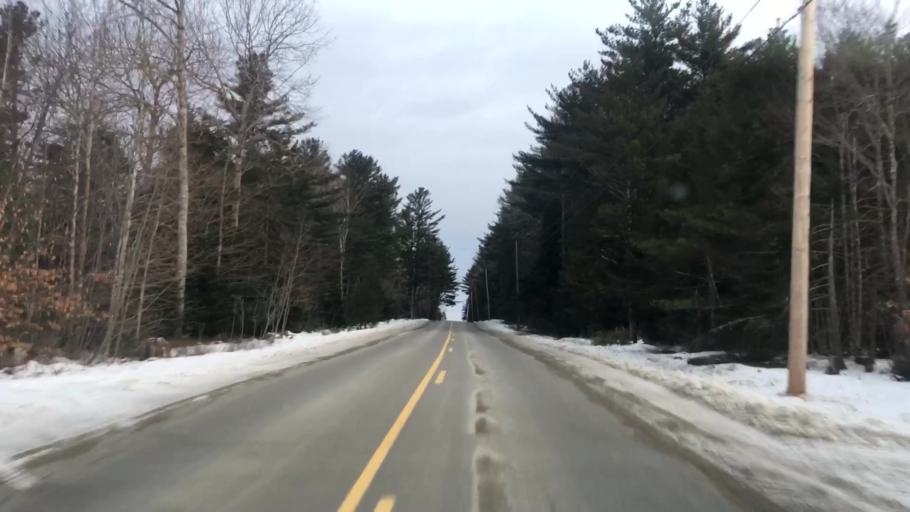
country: US
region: Maine
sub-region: Hancock County
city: Franklin
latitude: 44.7636
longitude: -68.3251
